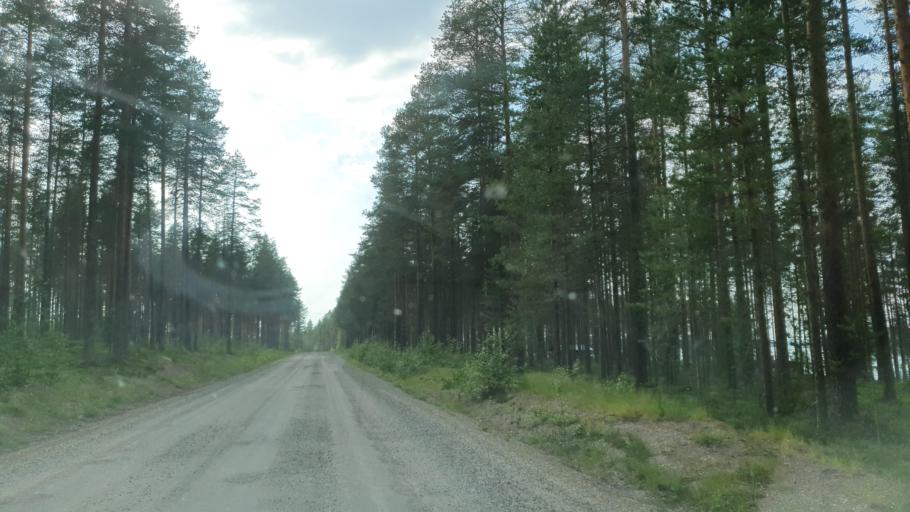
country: FI
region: Kainuu
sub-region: Kehys-Kainuu
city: Kuhmo
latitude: 64.0950
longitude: 29.6402
